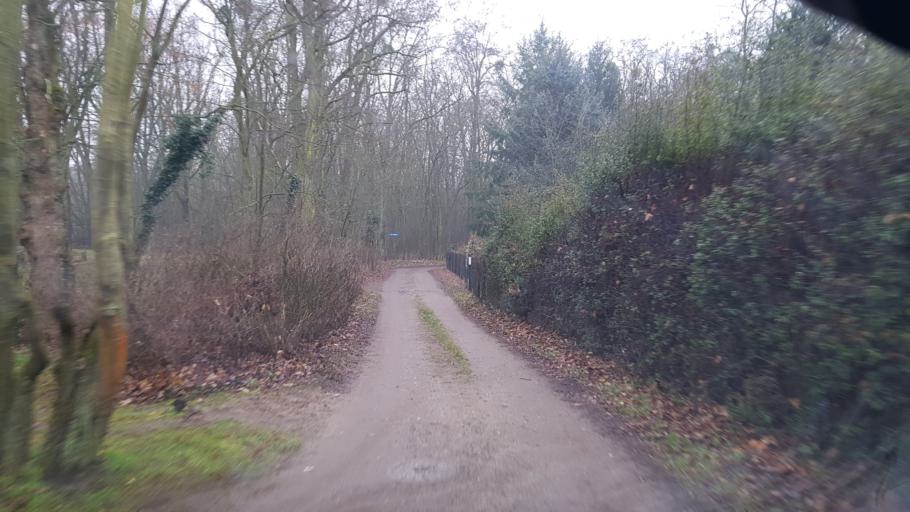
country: DE
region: Brandenburg
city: Stahnsdorf
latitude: 52.3594
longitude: 13.1950
